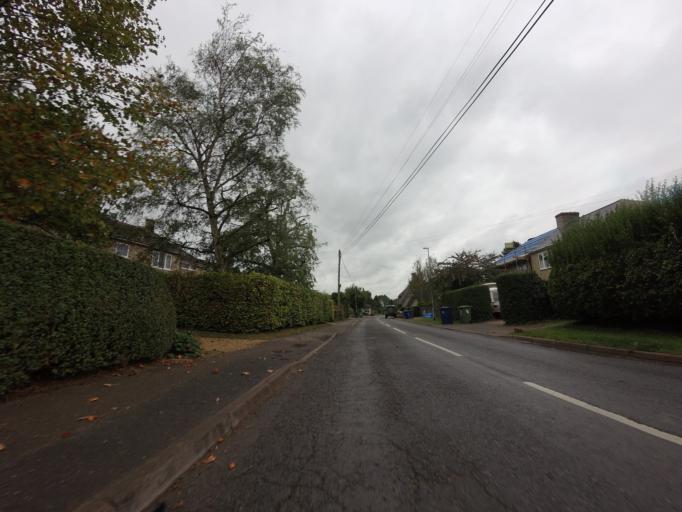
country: GB
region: England
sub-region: Cambridgeshire
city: Haslingfield
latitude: 52.1522
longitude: 0.0217
